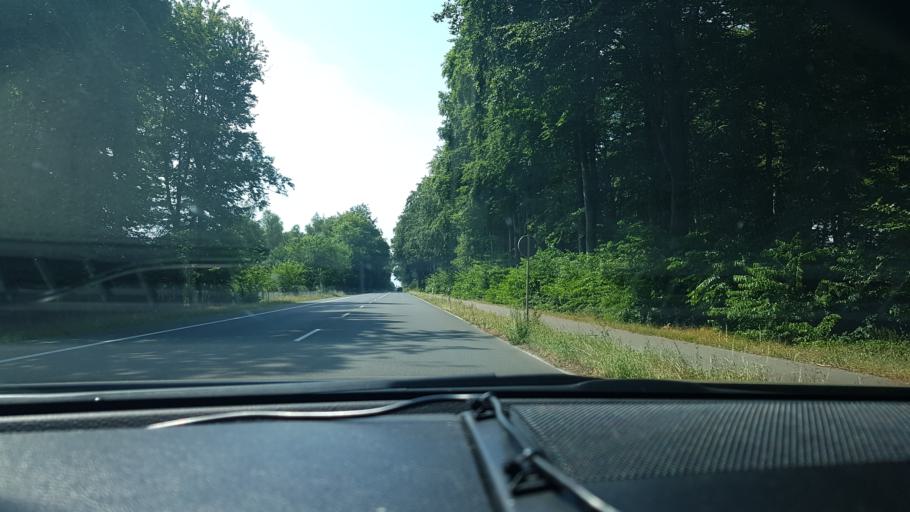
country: DE
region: North Rhine-Westphalia
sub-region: Regierungsbezirk Dusseldorf
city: Bruggen
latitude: 51.2084
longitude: 6.1204
